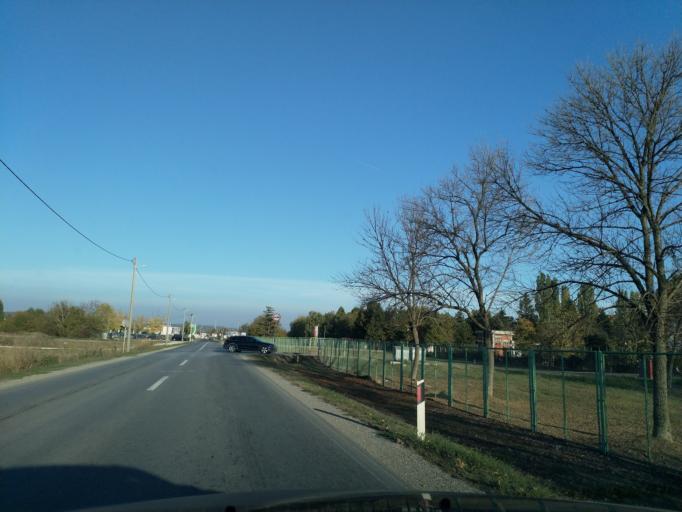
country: RS
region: Central Serbia
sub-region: Pomoravski Okrug
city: Svilajnac
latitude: 44.2275
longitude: 21.1682
